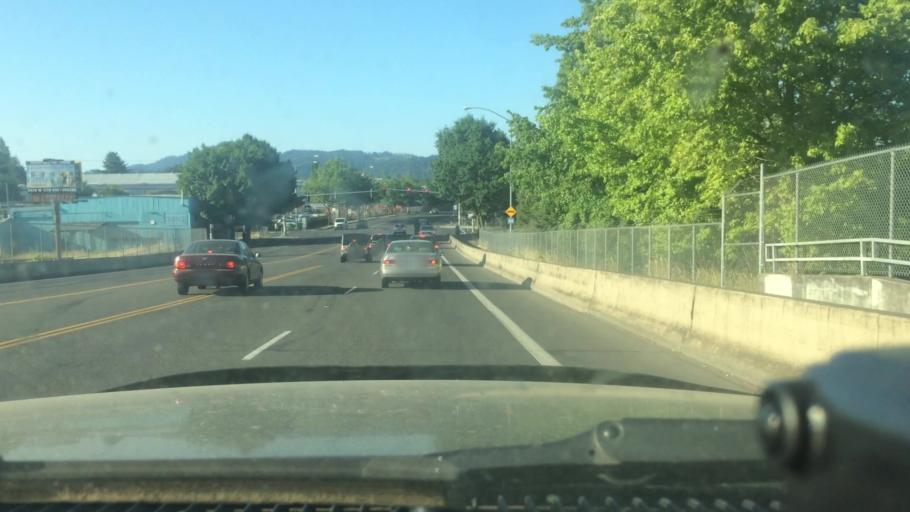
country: US
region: Oregon
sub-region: Lane County
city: Eugene
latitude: 44.0588
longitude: -123.1175
